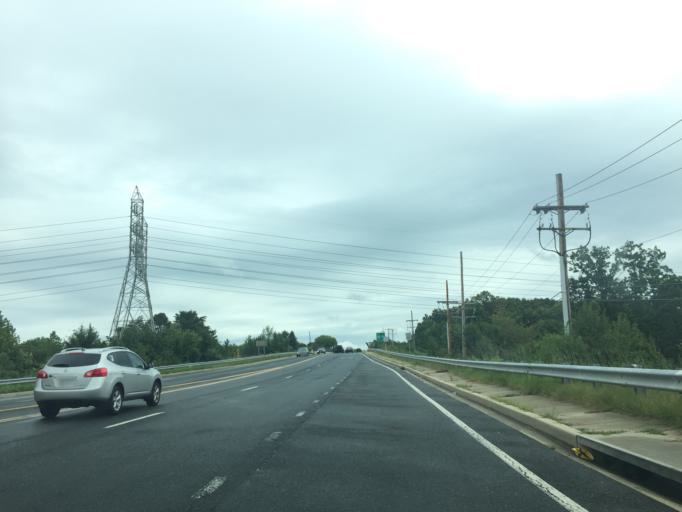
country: US
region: Maryland
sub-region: Baltimore County
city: White Marsh
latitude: 39.3755
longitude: -76.4403
